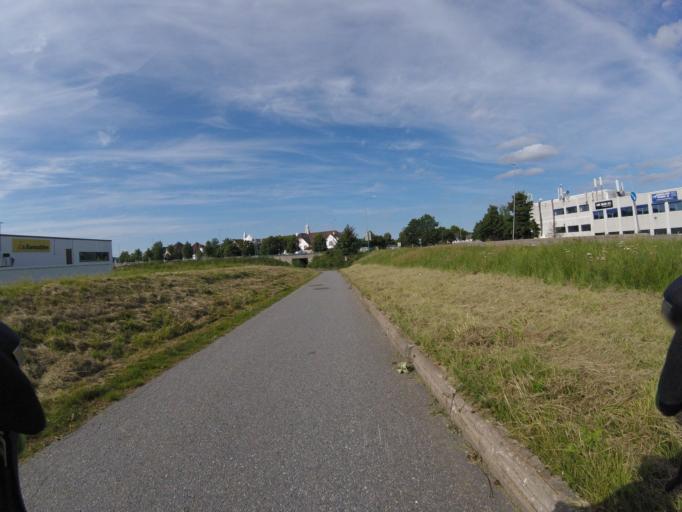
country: NO
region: Akershus
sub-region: Skedsmo
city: Lillestrom
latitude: 59.9777
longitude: 11.0010
